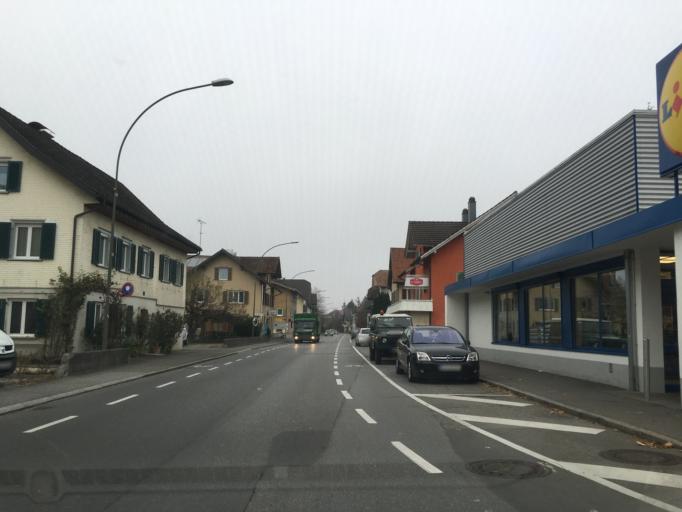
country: AT
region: Vorarlberg
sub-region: Politischer Bezirk Dornbirn
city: Lustenau
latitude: 47.4210
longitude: 9.6601
